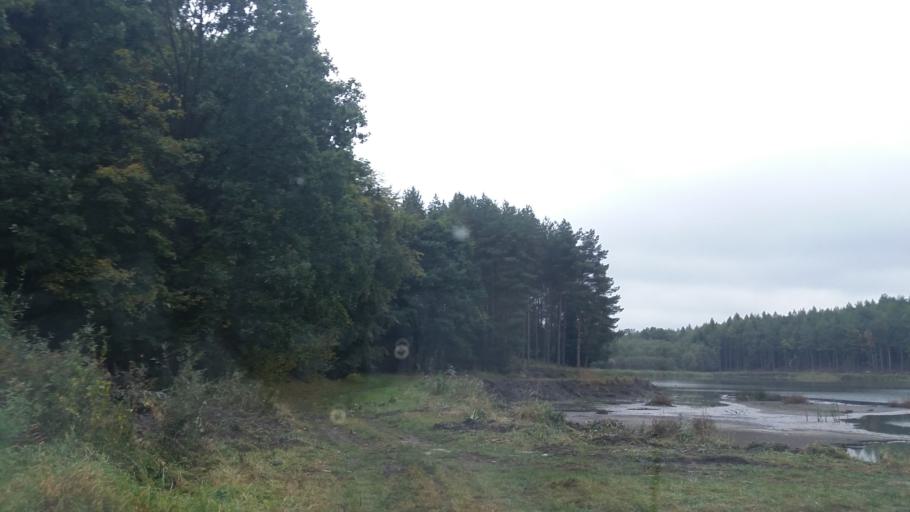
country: PL
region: West Pomeranian Voivodeship
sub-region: Powiat choszczenski
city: Pelczyce
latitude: 53.0703
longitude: 15.2819
